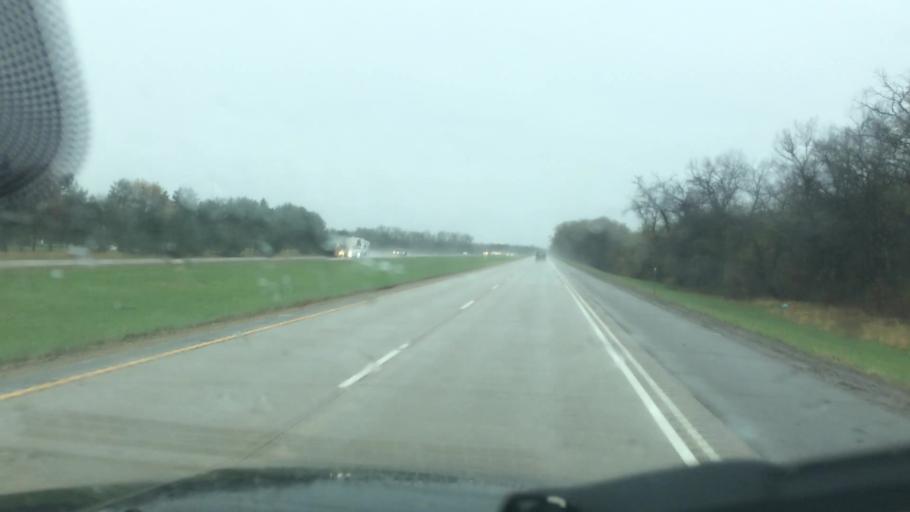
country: US
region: Wisconsin
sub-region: Portage County
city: Stevens Point
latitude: 44.6561
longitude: -89.6413
